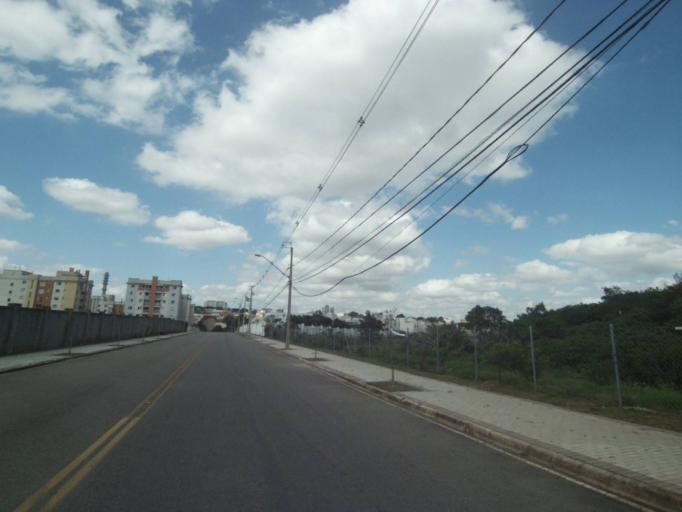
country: BR
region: Parana
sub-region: Curitiba
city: Curitiba
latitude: -25.5054
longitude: -49.3099
